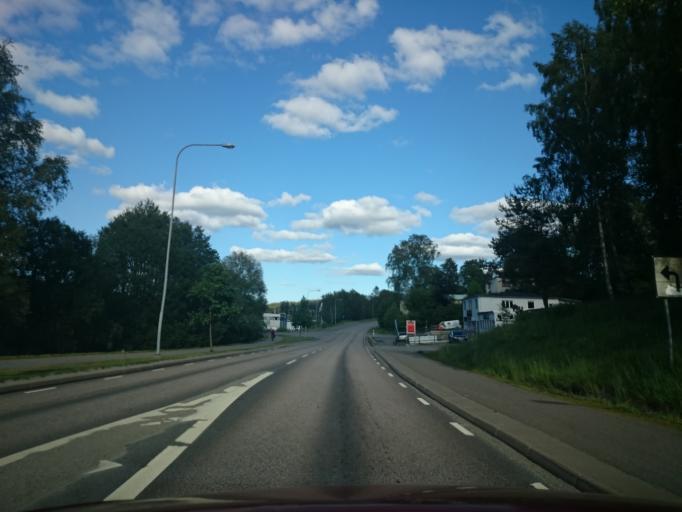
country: SE
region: Vaestra Goetaland
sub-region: Harryda Kommun
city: Molnlycke
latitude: 57.6675
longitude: 12.1067
